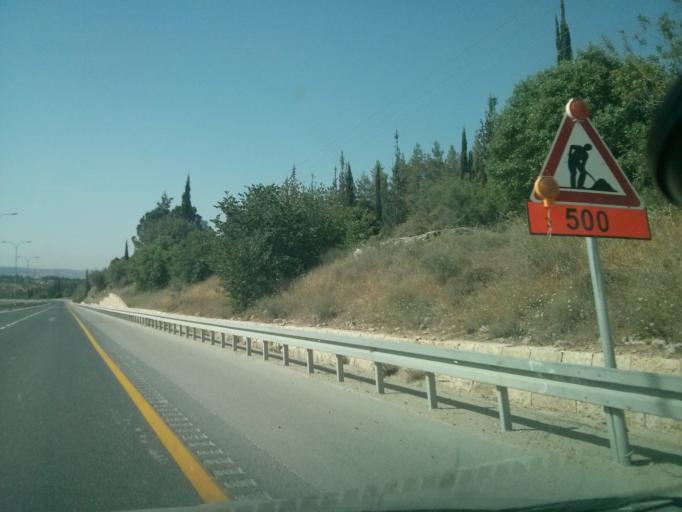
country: IL
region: Jerusalem
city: Bet Shemesh
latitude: 31.7023
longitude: 35.0085
